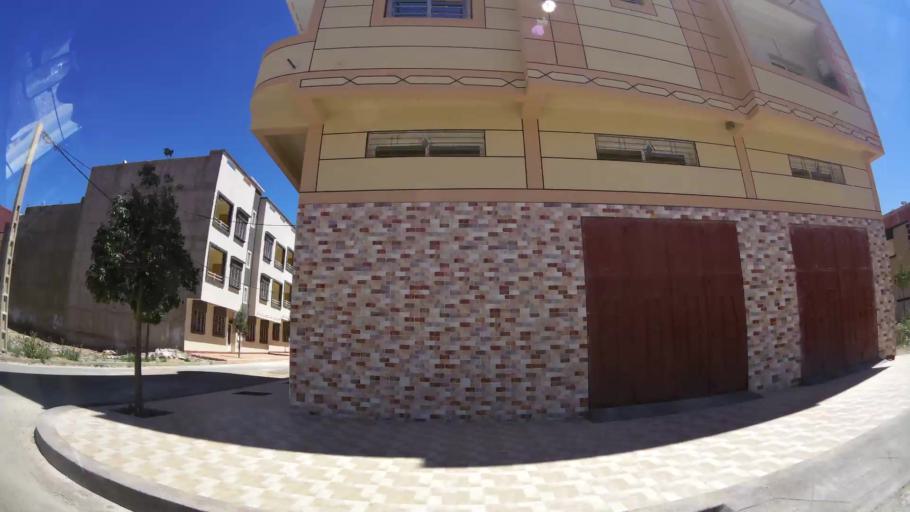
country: MA
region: Oriental
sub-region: Oujda-Angad
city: Oujda
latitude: 34.6859
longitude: -1.8707
